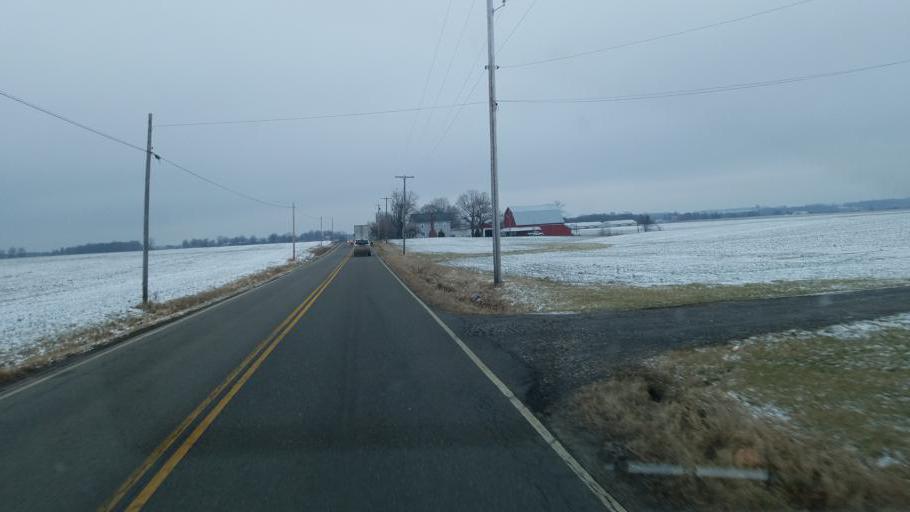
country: US
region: Ohio
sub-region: Wayne County
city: Smithville
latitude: 40.8172
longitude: -81.8436
